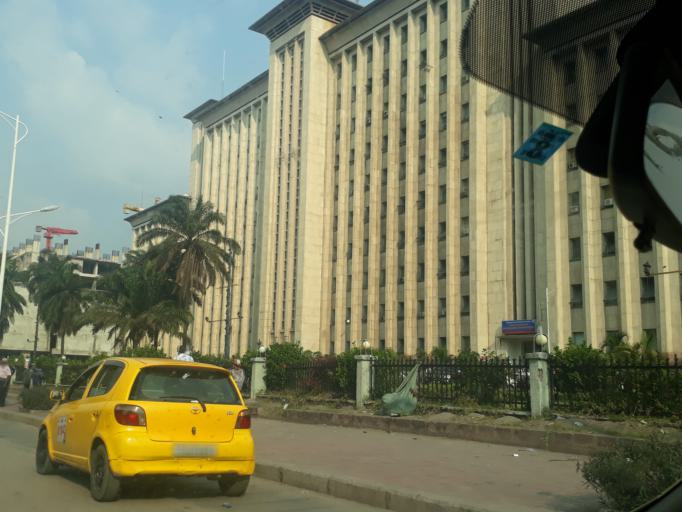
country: CD
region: Kinshasa
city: Kinshasa
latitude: -4.3024
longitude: 15.3140
